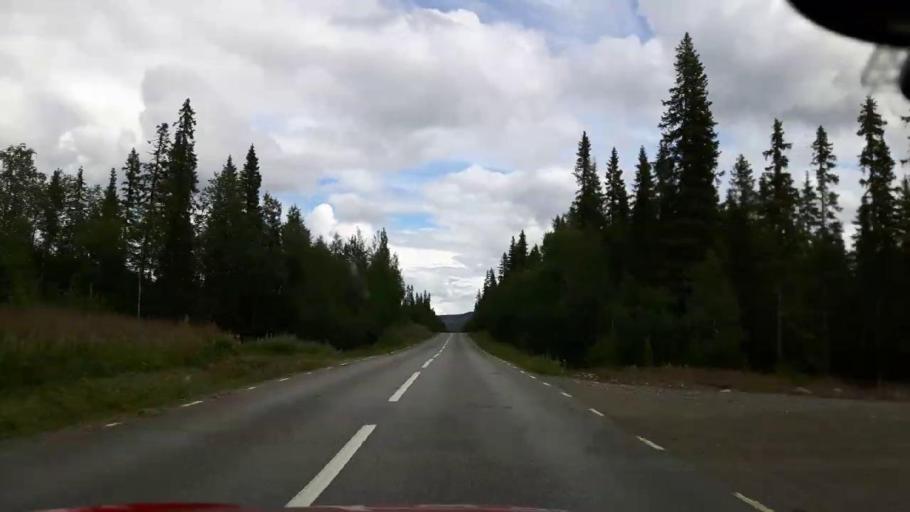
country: NO
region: Nord-Trondelag
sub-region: Lierne
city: Sandvika
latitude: 64.3901
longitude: 14.4486
